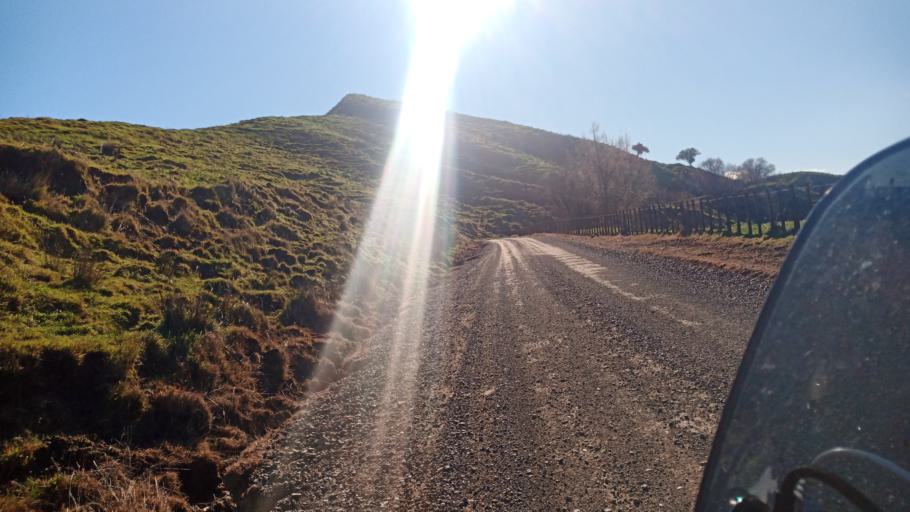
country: NZ
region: Hawke's Bay
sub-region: Wairoa District
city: Wairoa
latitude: -38.7776
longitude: 177.2634
